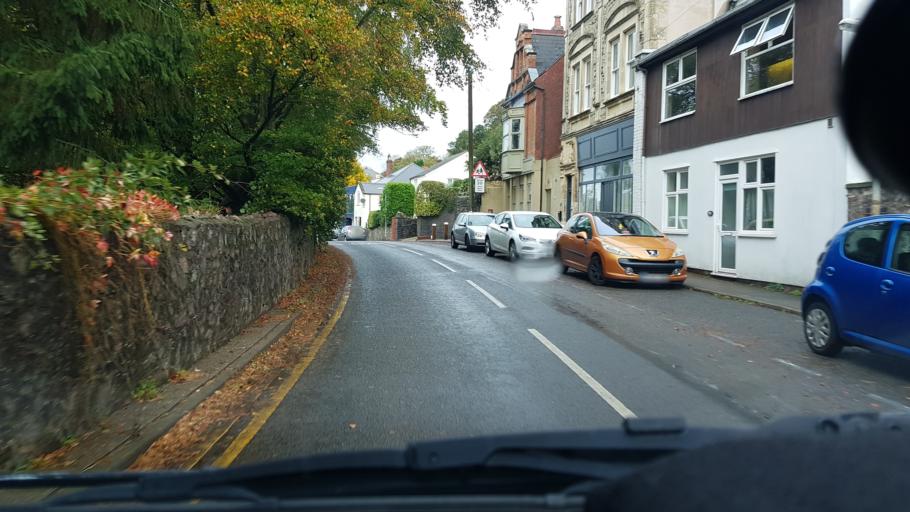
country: GB
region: England
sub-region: Worcestershire
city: Great Malvern
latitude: 52.1116
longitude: -2.3461
